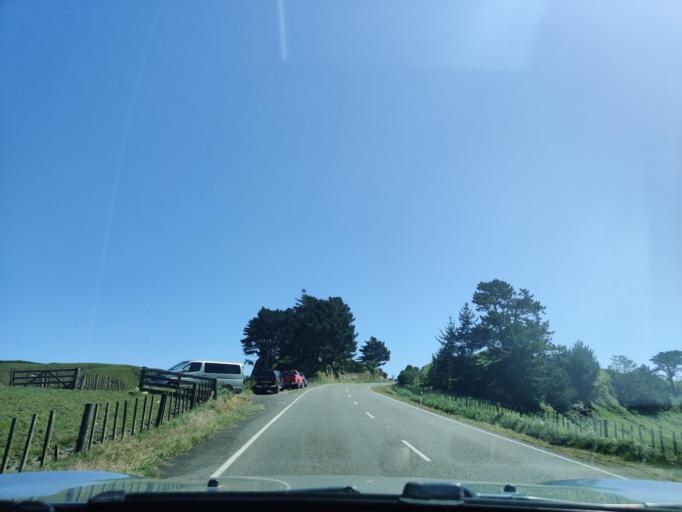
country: NZ
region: Taranaki
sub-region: South Taranaki District
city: Patea
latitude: -39.7559
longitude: 174.5404
